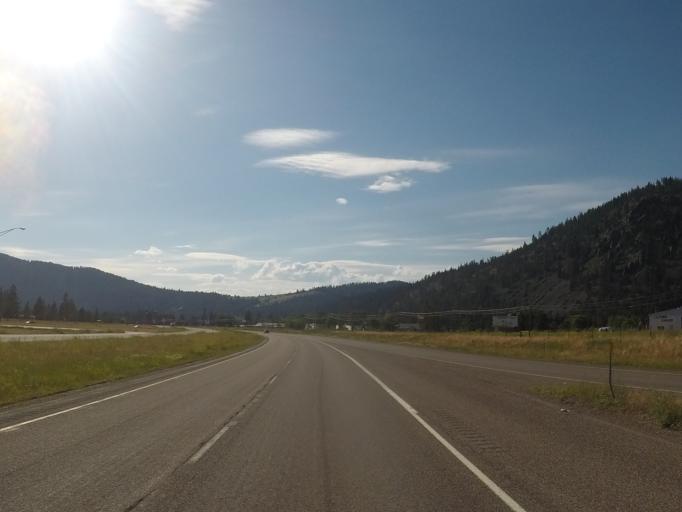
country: US
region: Montana
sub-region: Missoula County
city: Bonner-West Riverside
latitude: 46.8777
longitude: -113.8948
